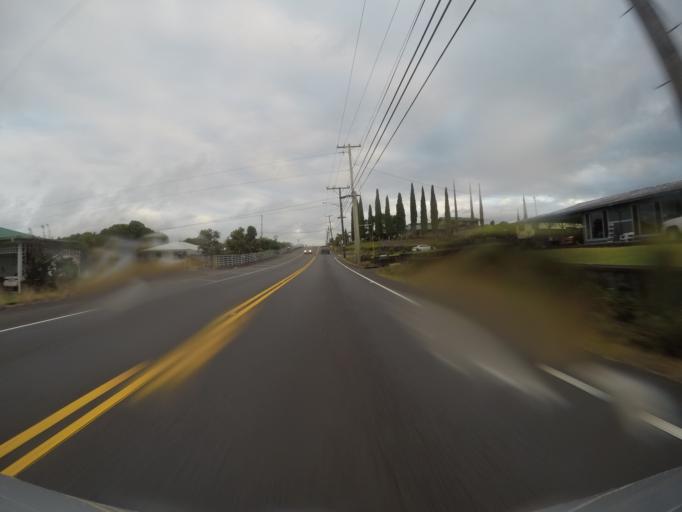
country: US
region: Hawaii
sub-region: Hawaii County
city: Hilo
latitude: 19.6872
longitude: -155.0900
